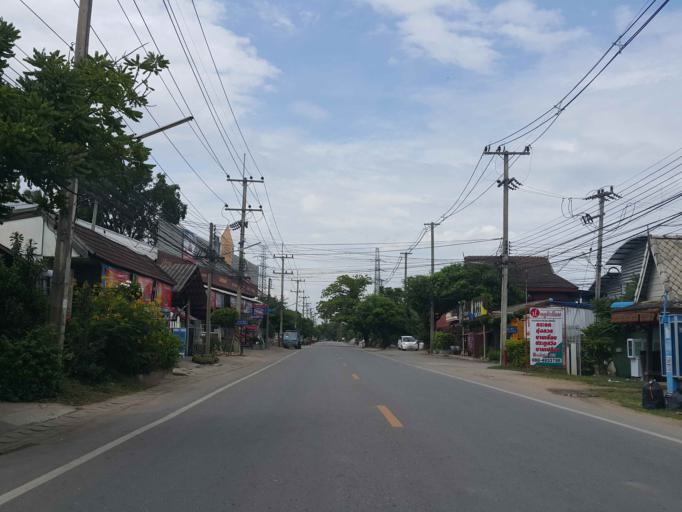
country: TH
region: Lamphun
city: Lamphun
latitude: 18.6288
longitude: 99.0384
